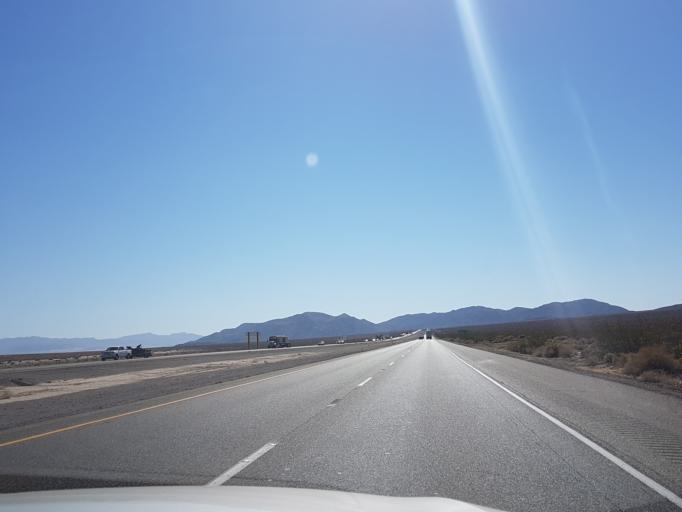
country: US
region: California
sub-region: San Bernardino County
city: Fort Irwin
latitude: 35.2470
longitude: -116.0936
